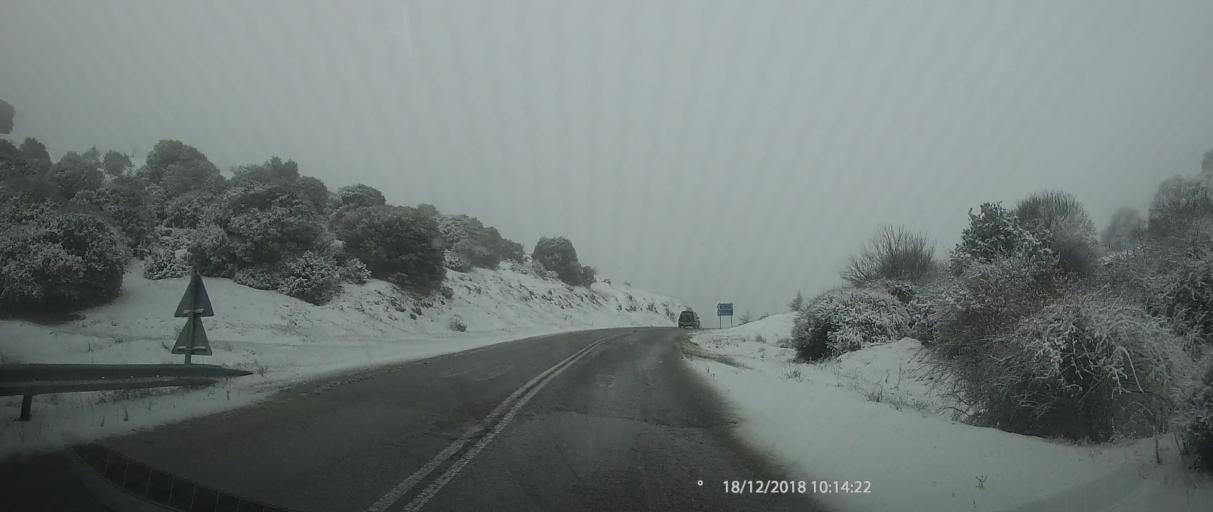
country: GR
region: Thessaly
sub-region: Nomos Larisis
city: Livadi
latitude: 40.1080
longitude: 22.2030
